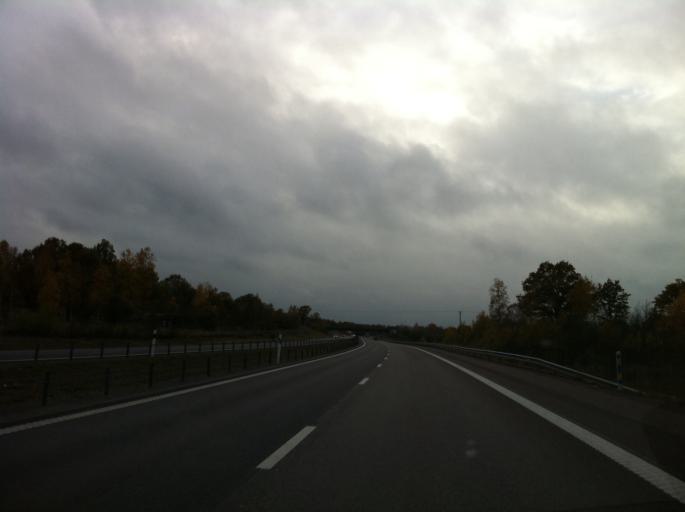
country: SE
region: OEstergoetland
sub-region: Odeshogs Kommun
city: OEdeshoeg
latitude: 58.2379
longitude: 14.7161
